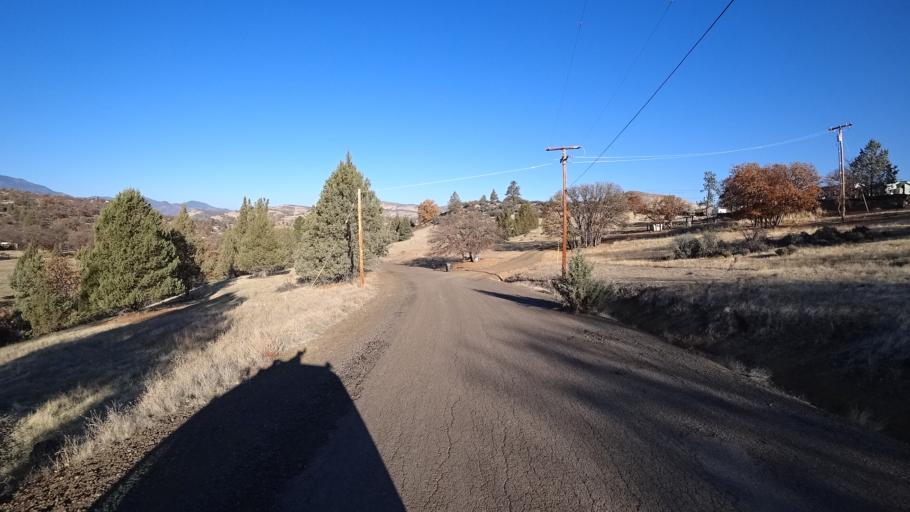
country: US
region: California
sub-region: Siskiyou County
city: Montague
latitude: 41.8923
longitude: -122.4982
